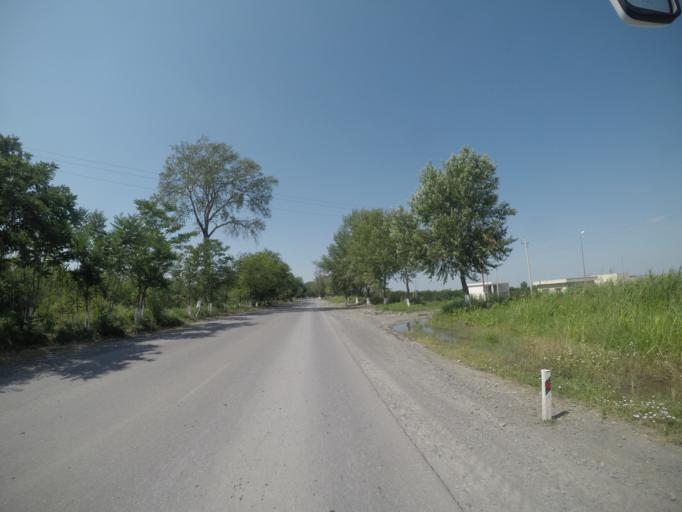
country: AZ
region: Agdas
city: Agdas
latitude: 40.6949
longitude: 47.5398
